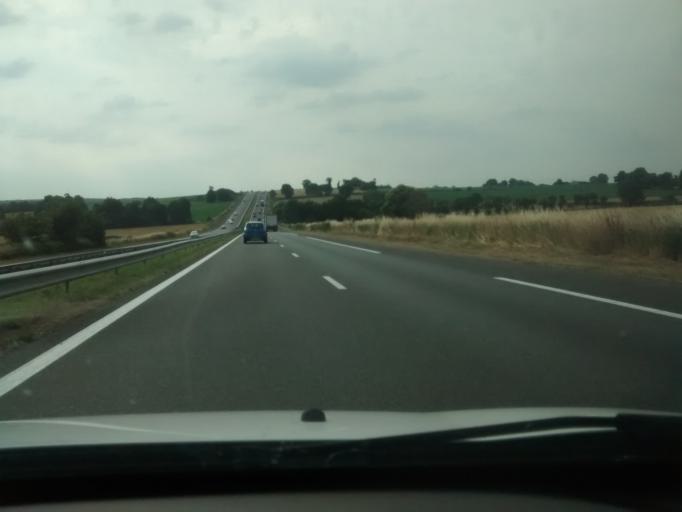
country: FR
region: Brittany
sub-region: Departement d'Ille-et-Vilaine
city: Montauban-de-Bretagne
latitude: 48.2149
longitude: -2.0928
